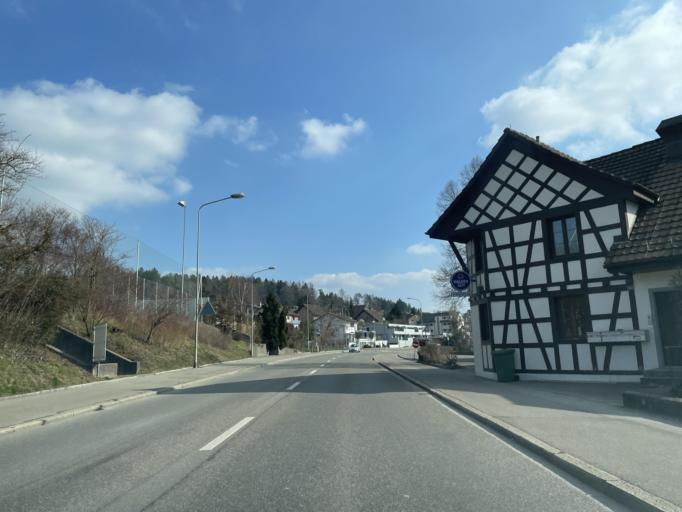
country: CH
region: Zurich
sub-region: Bezirk Winterthur
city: Veltheim (Kreis 5) / Rosenberg
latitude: 47.5281
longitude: 8.7113
